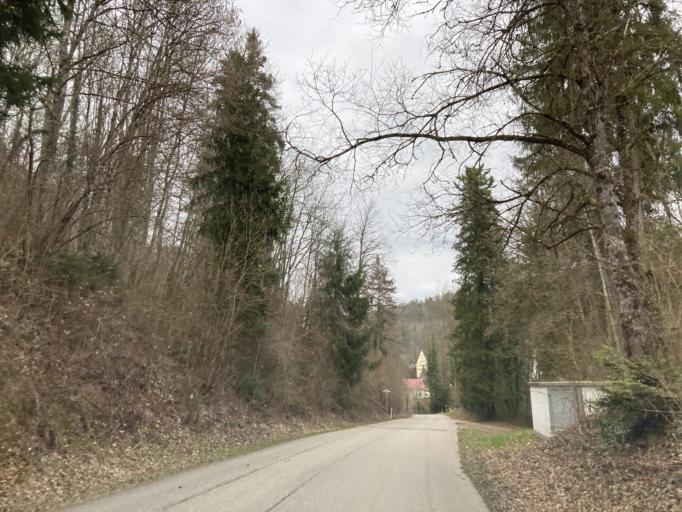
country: DE
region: Baden-Wuerttemberg
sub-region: Tuebingen Region
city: Hirrlingen
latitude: 48.4507
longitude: 8.9009
